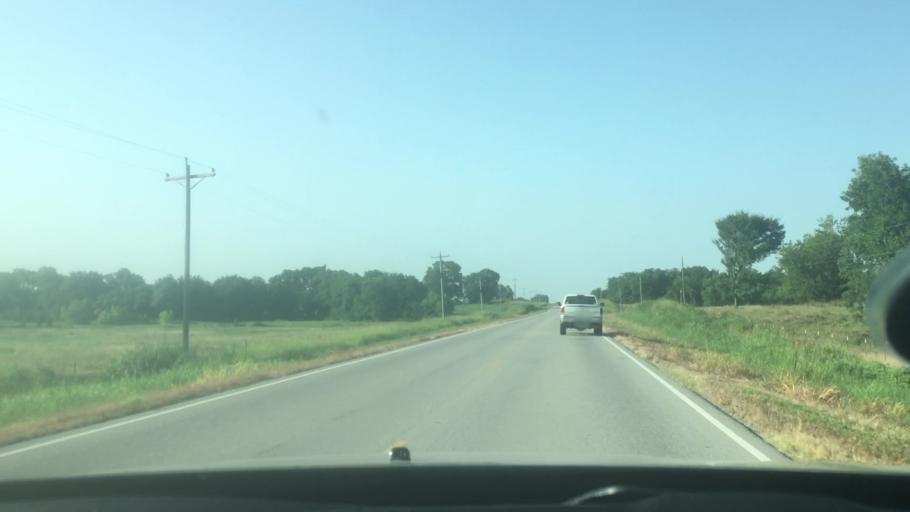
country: US
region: Oklahoma
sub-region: Coal County
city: Coalgate
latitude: 34.4601
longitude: -96.4246
